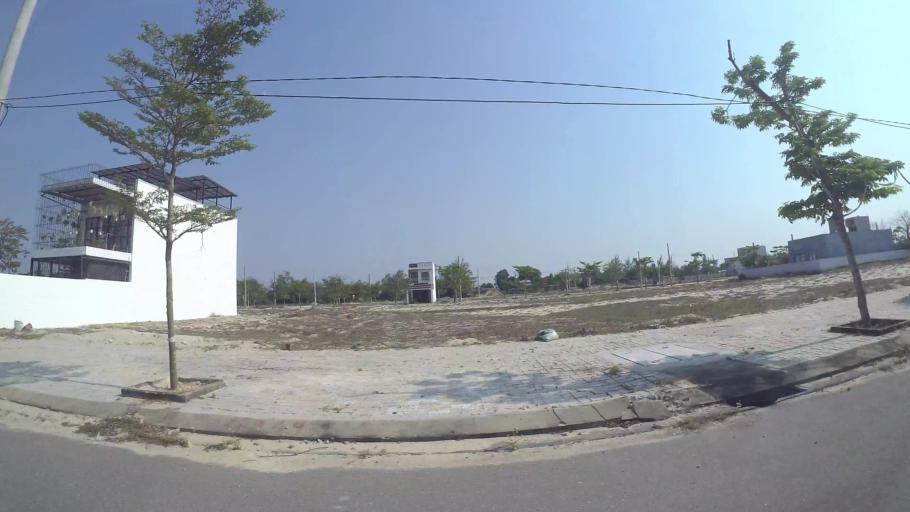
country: VN
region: Da Nang
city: Ngu Hanh Son
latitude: 15.9550
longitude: 108.2760
